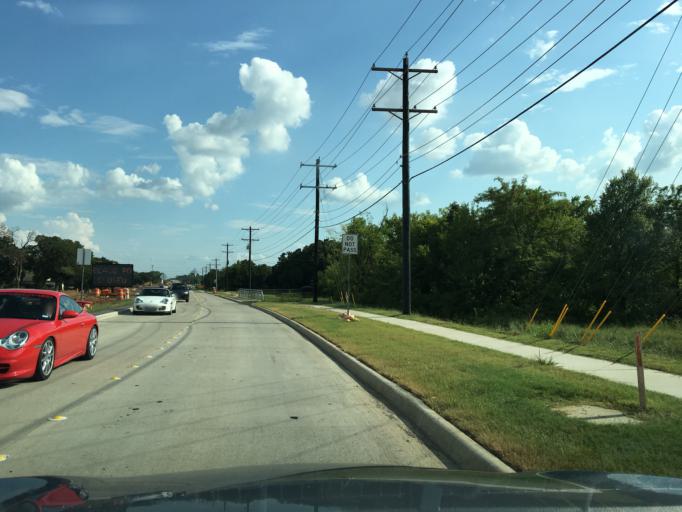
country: US
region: Texas
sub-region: Denton County
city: Denton
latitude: 33.2321
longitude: -97.0827
